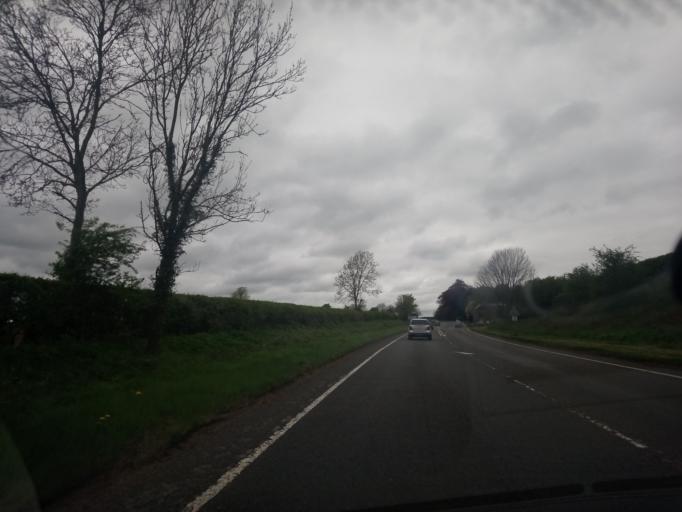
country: GB
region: England
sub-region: Telford and Wrekin
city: Chetwynd
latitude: 52.8124
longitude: -2.4424
